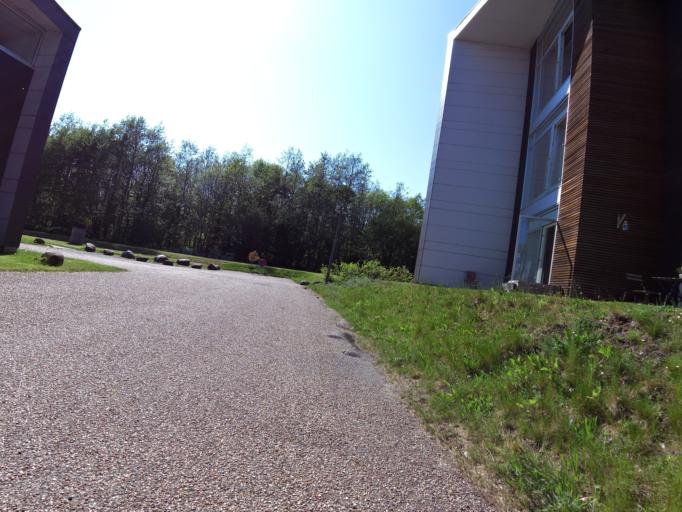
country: DK
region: Central Jutland
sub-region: Arhus Kommune
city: Stavtrup
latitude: 56.1492
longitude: 10.1440
